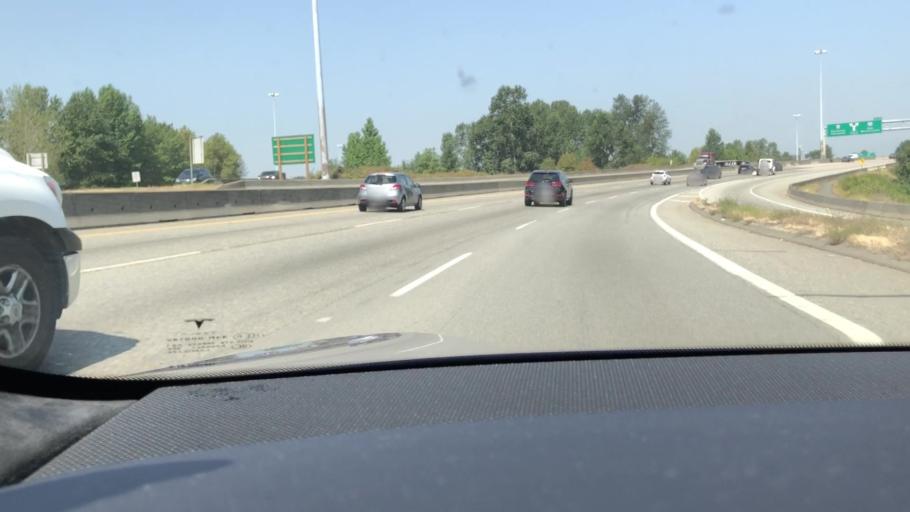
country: CA
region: British Columbia
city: New Westminster
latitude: 49.1725
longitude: -122.9536
